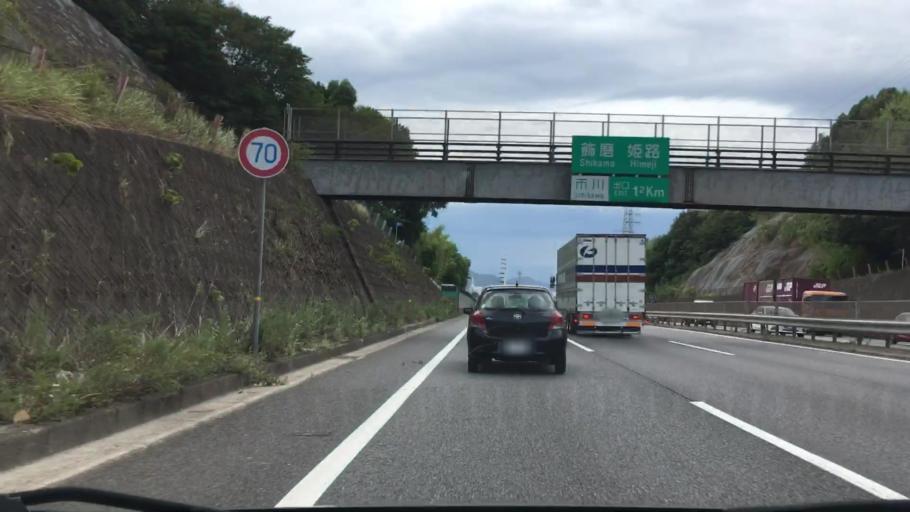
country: JP
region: Hyogo
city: Himeji
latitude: 34.8026
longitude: 134.7065
